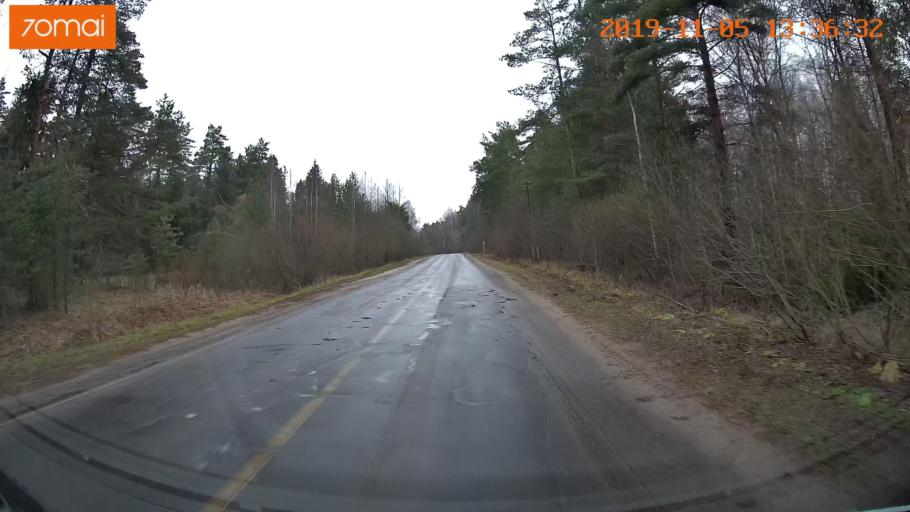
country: RU
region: Ivanovo
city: Shuya
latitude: 56.9153
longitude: 41.3823
